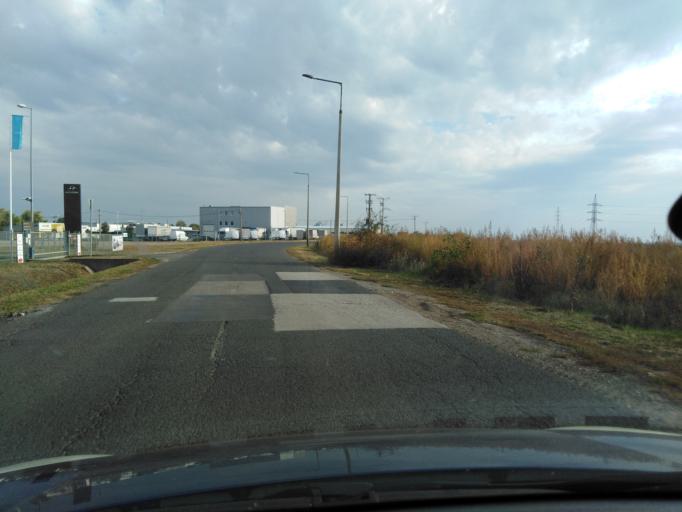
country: HU
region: Heves
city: Hatvan
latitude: 47.6662
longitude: 19.6424
